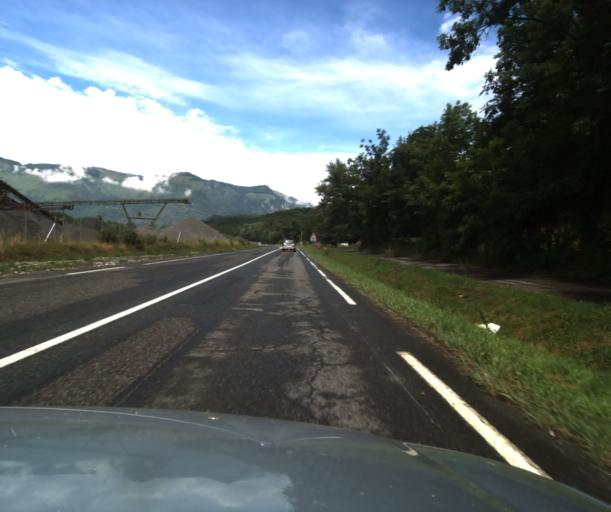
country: FR
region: Midi-Pyrenees
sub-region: Departement des Hautes-Pyrenees
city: Argeles-Gazost
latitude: 42.9965
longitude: -0.0776
